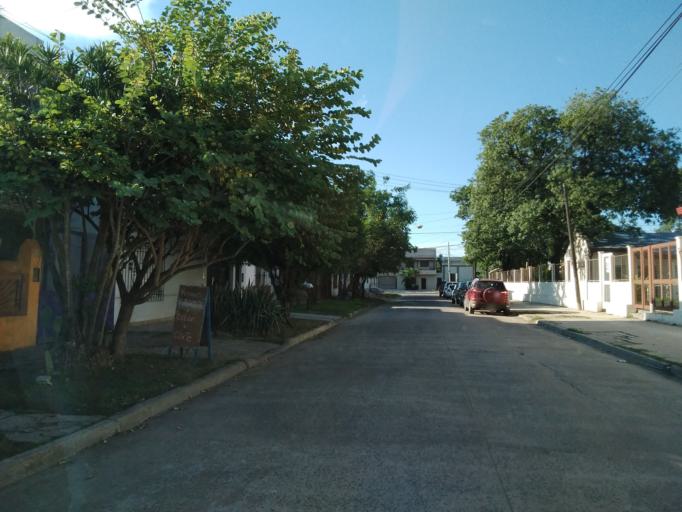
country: AR
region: Corrientes
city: Corrientes
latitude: -27.4722
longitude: -58.8118
